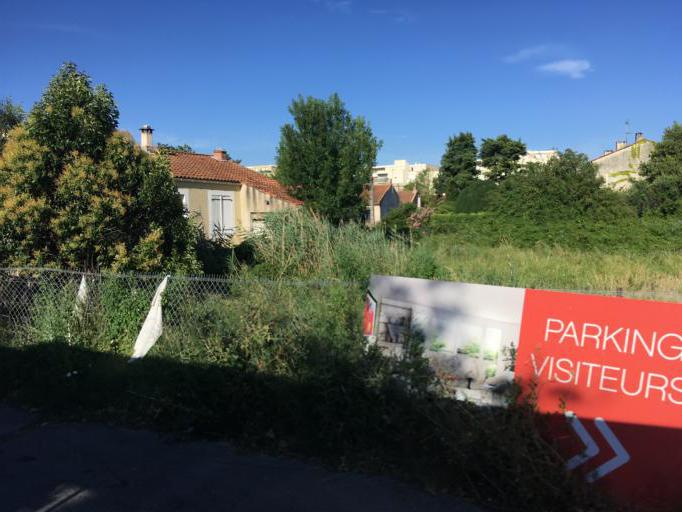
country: FR
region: Provence-Alpes-Cote d'Azur
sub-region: Departement du Vaucluse
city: Avignon
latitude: 43.9432
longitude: 4.8275
